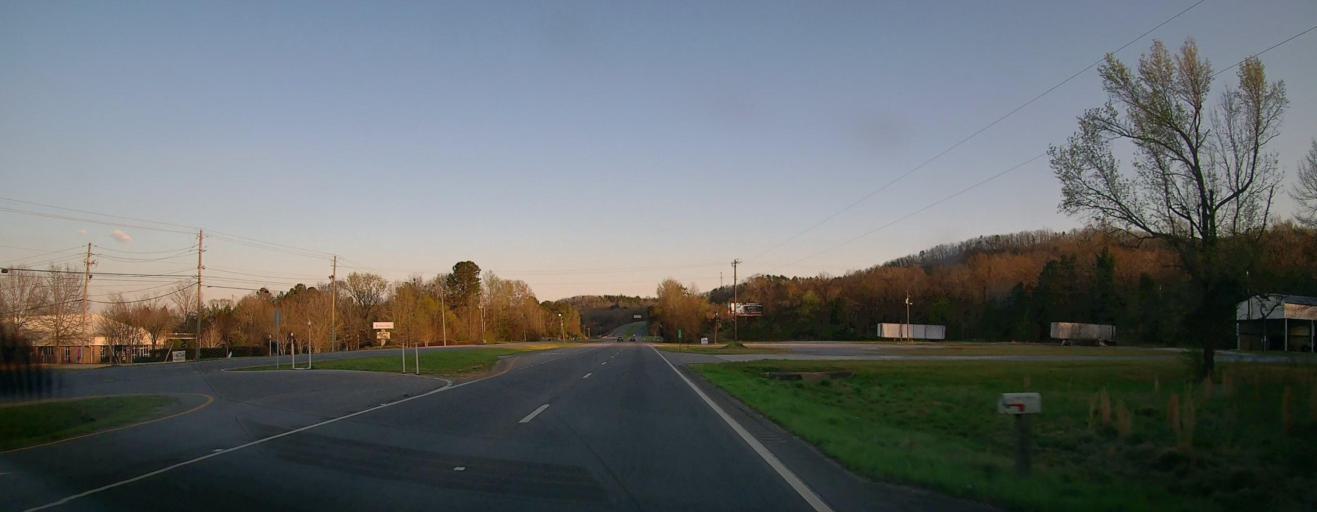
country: US
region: Alabama
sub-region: Talladega County
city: Mignon
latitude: 33.2126
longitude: -86.3137
